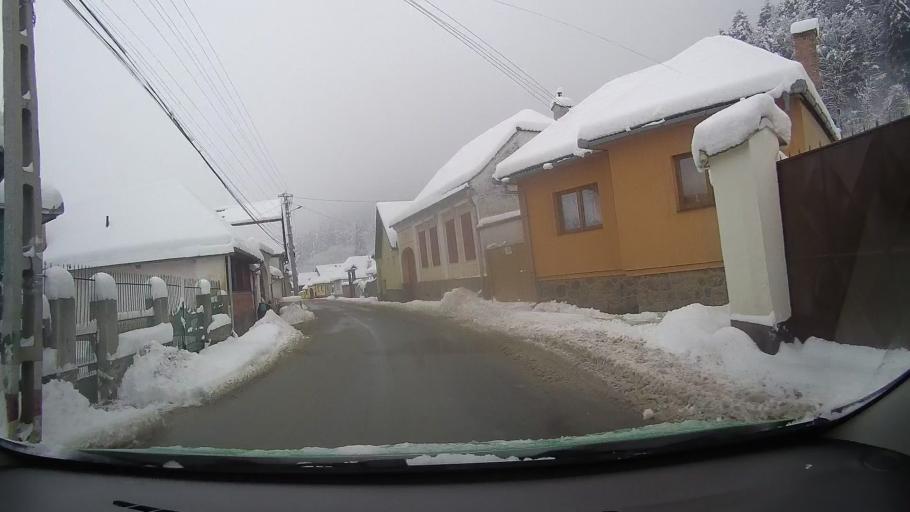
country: RO
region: Sibiu
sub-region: Comuna Tilisca
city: Tilisca
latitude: 45.7971
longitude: 23.8667
